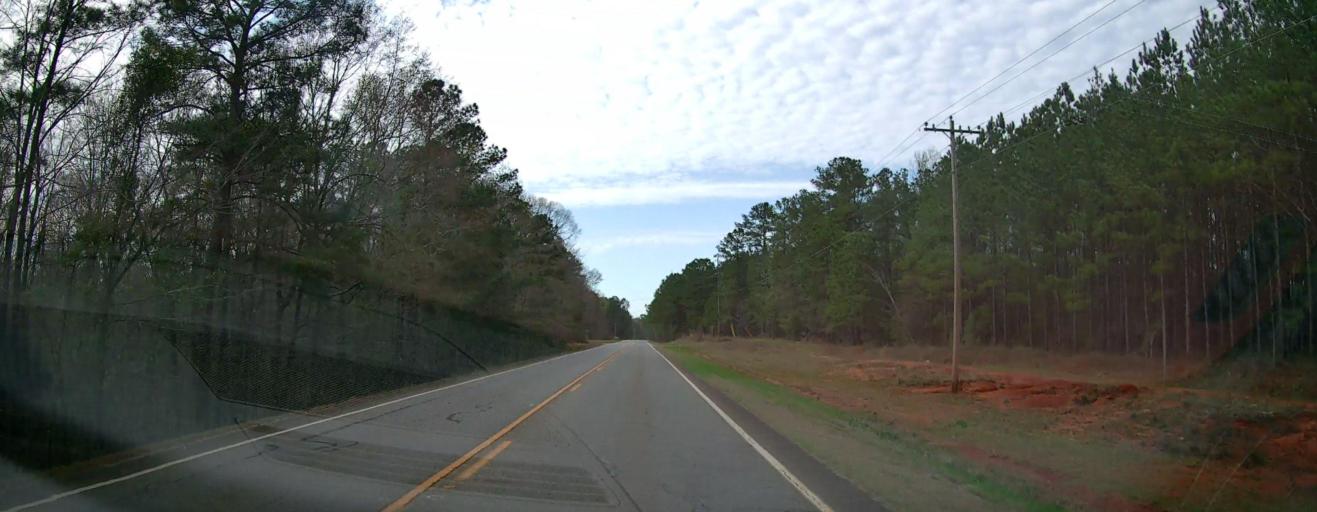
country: US
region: Georgia
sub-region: Jones County
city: Gray
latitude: 32.9851
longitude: -83.6753
